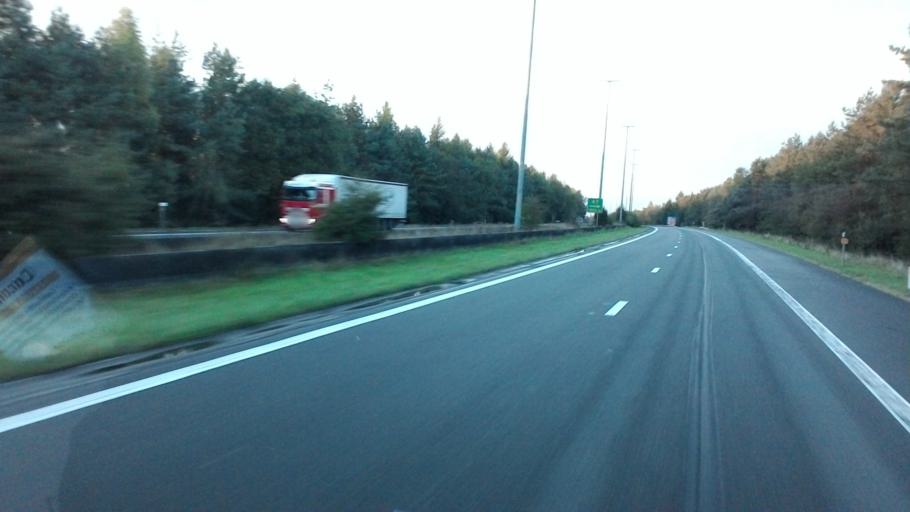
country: BE
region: Wallonia
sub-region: Province de Liege
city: Aywaille
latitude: 50.4092
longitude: 5.7071
